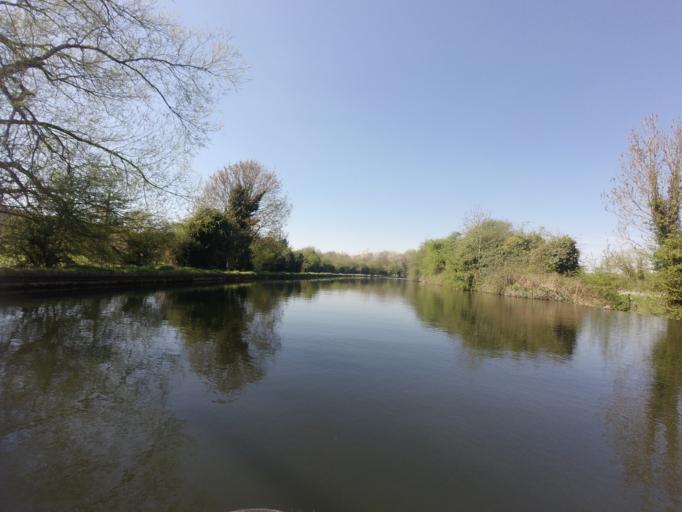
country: GB
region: England
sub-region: Hertfordshire
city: Kings Langley
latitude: 51.6998
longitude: -0.4392
